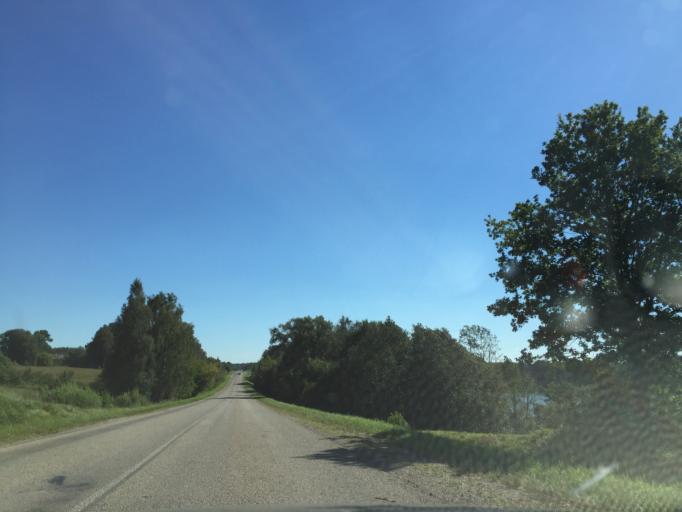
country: LV
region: Akniste
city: Akniste
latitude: 56.0276
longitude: 25.9162
